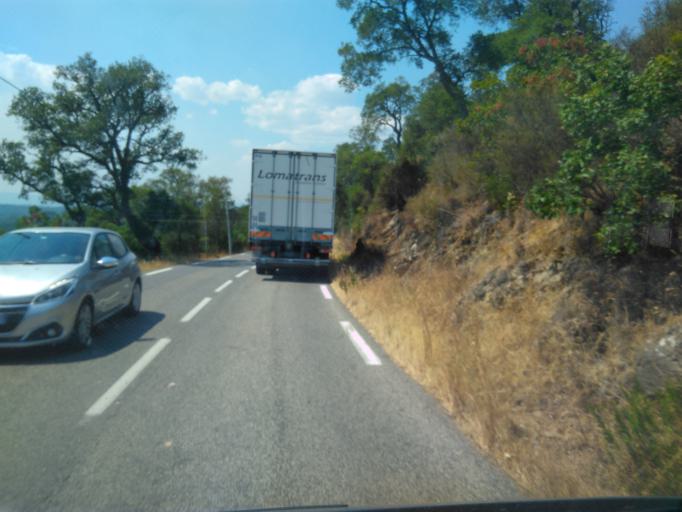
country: FR
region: Provence-Alpes-Cote d'Azur
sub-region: Departement du Var
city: La Garde-Freinet
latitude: 43.3324
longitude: 6.4349
